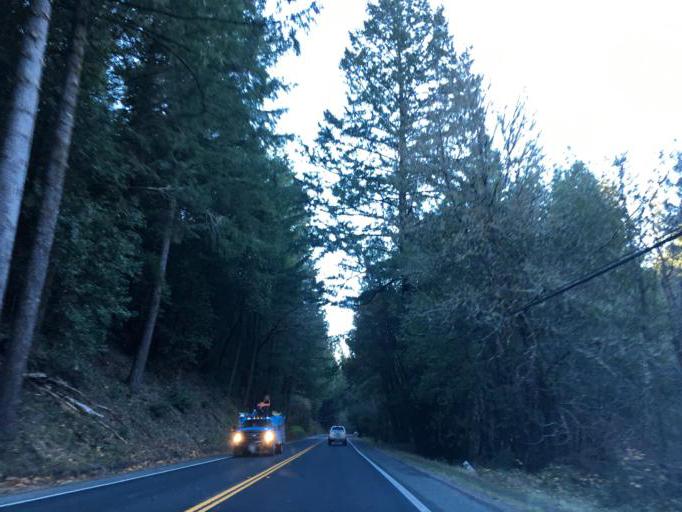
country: US
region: California
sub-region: Mendocino County
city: Brooktrails
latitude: 39.5081
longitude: -123.3829
